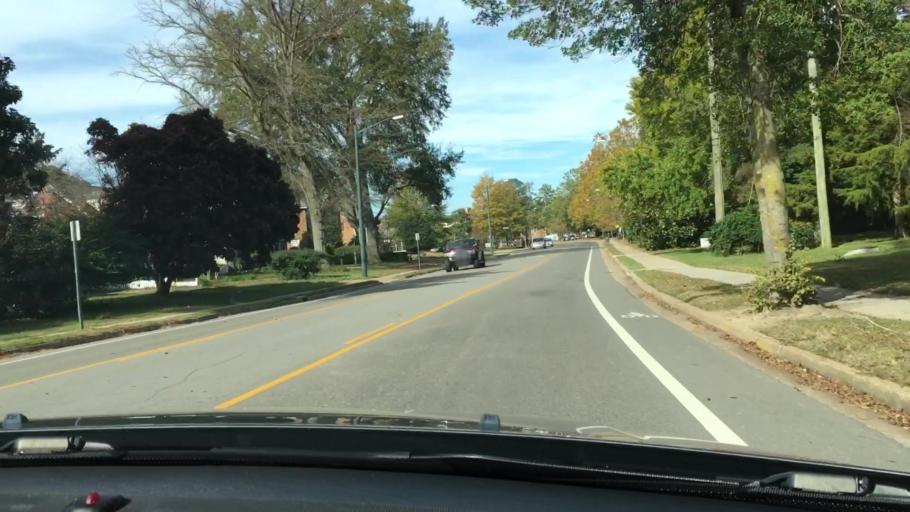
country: US
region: Virginia
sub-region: City of Williamsburg
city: Williamsburg
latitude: 37.2768
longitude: -76.7155
